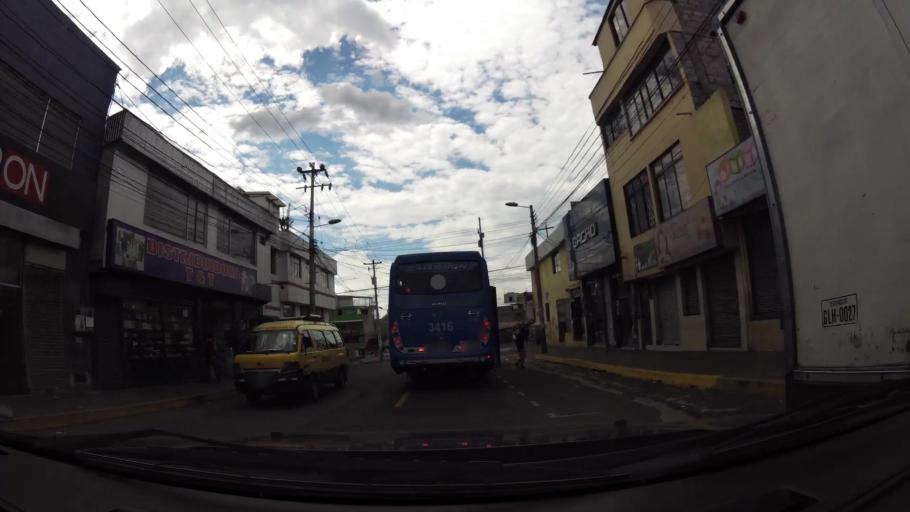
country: EC
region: Pichincha
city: Quito
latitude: -0.0925
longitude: -78.4529
